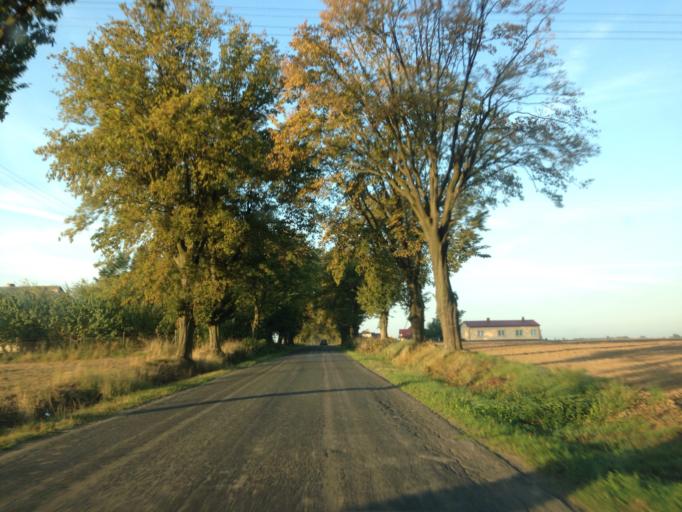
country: PL
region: Kujawsko-Pomorskie
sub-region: Powiat golubsko-dobrzynski
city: Radomin
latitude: 53.1181
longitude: 19.1595
